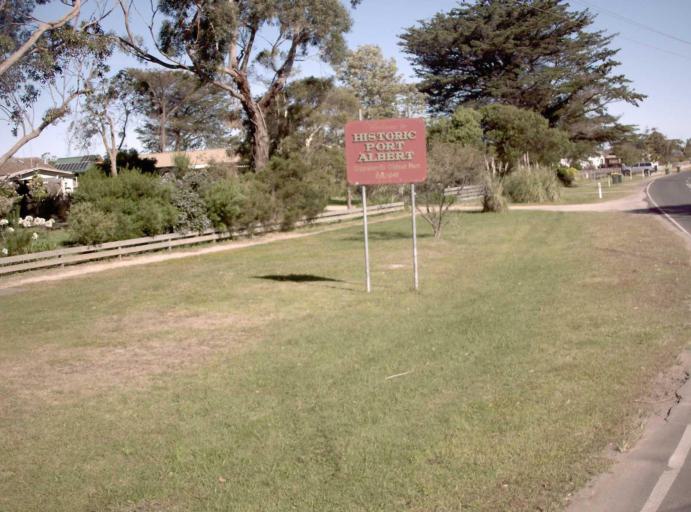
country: AU
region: Victoria
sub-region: Latrobe
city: Traralgon
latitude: -38.6657
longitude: 146.6886
